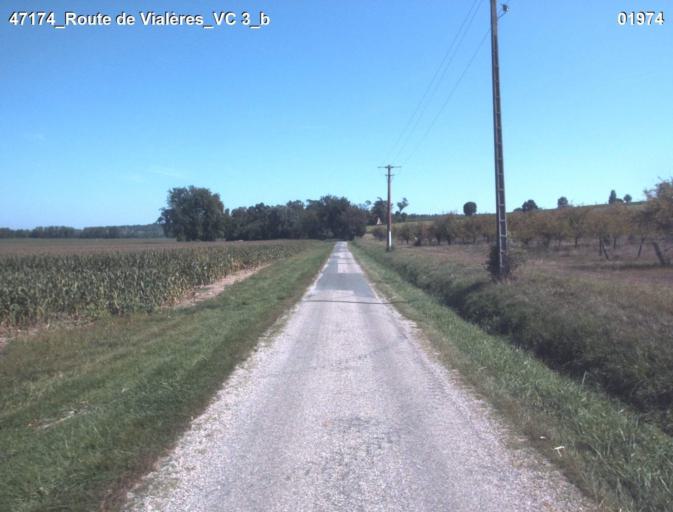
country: FR
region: Aquitaine
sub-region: Departement du Lot-et-Garonne
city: Nerac
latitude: 44.0507
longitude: 0.3820
